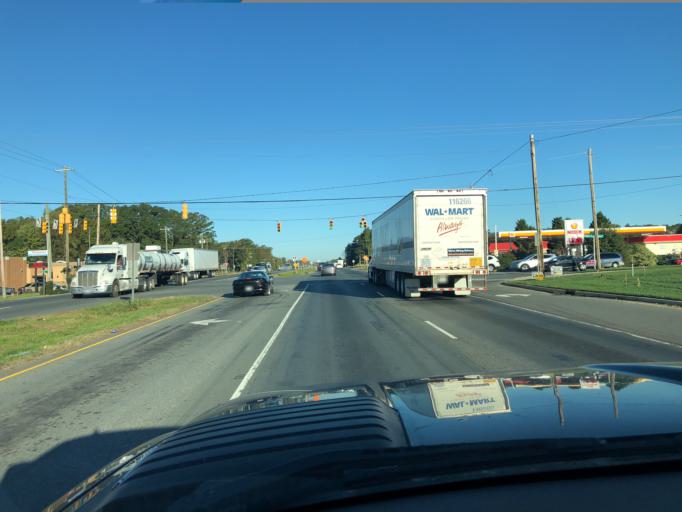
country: US
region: North Carolina
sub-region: Union County
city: Indian Trail
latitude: 35.0834
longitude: -80.6600
